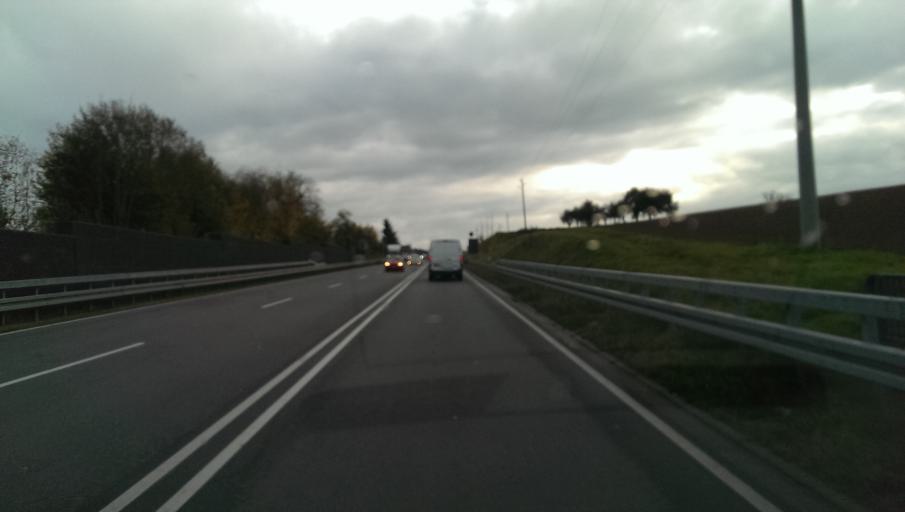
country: DE
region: Baden-Wuerttemberg
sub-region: Karlsruhe Region
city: Aglasterhausen
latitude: 49.3304
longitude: 8.9742
